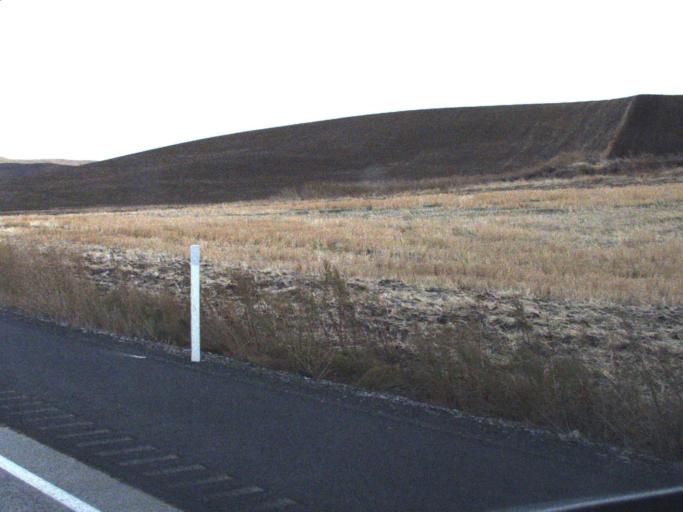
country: US
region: Washington
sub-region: Whitman County
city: Colfax
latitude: 46.9765
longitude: -117.3303
